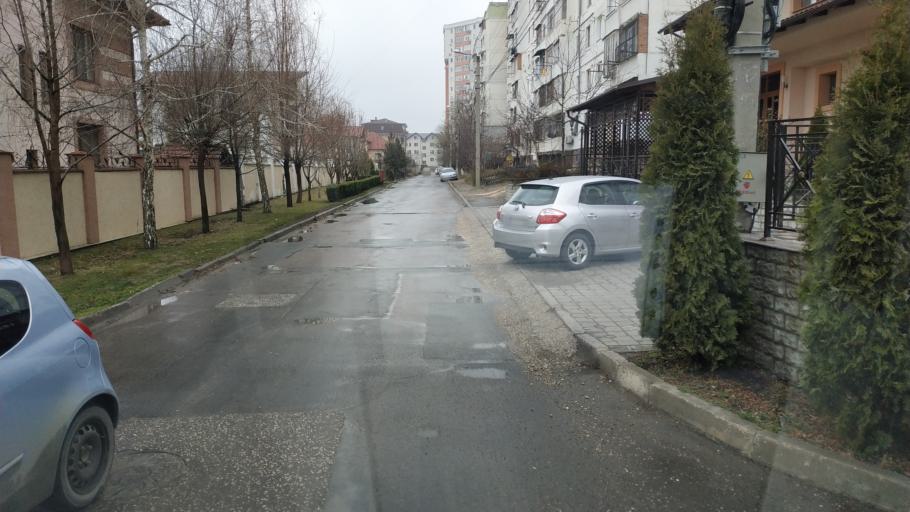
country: MD
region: Chisinau
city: Vatra
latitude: 47.0401
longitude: 28.7617
